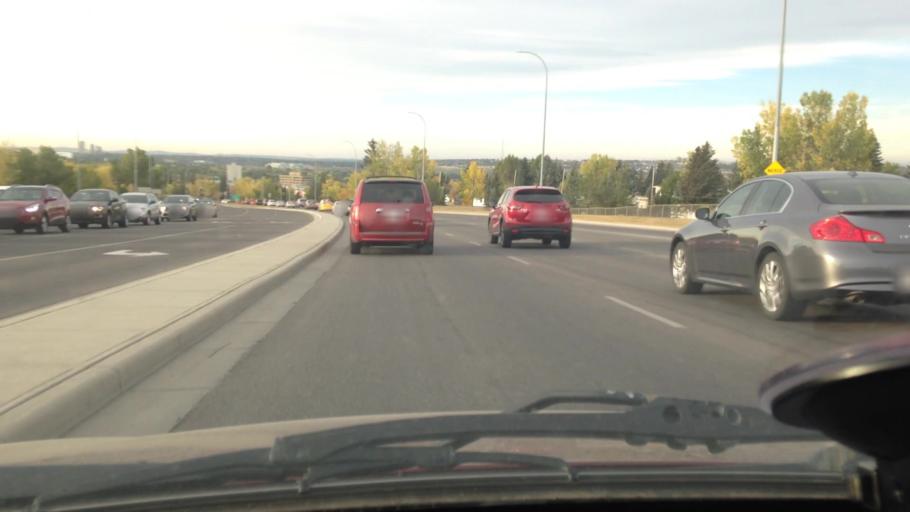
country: CA
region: Alberta
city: Calgary
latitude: 51.1087
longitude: -114.1403
